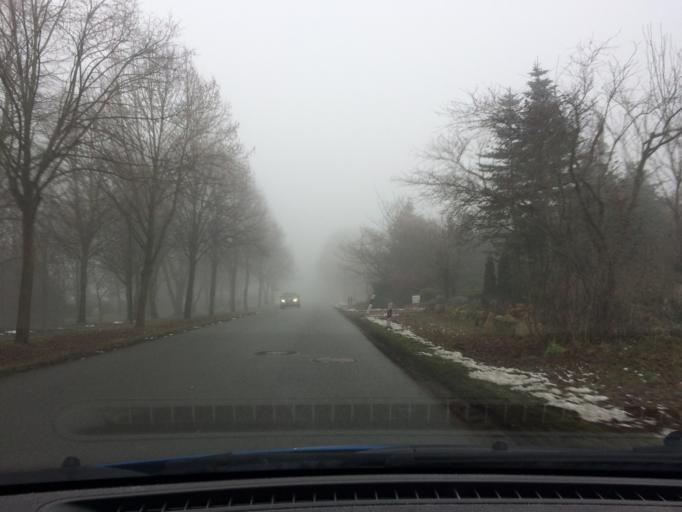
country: DE
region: Schleswig-Holstein
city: Lauenburg
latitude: 53.3813
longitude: 10.5443
